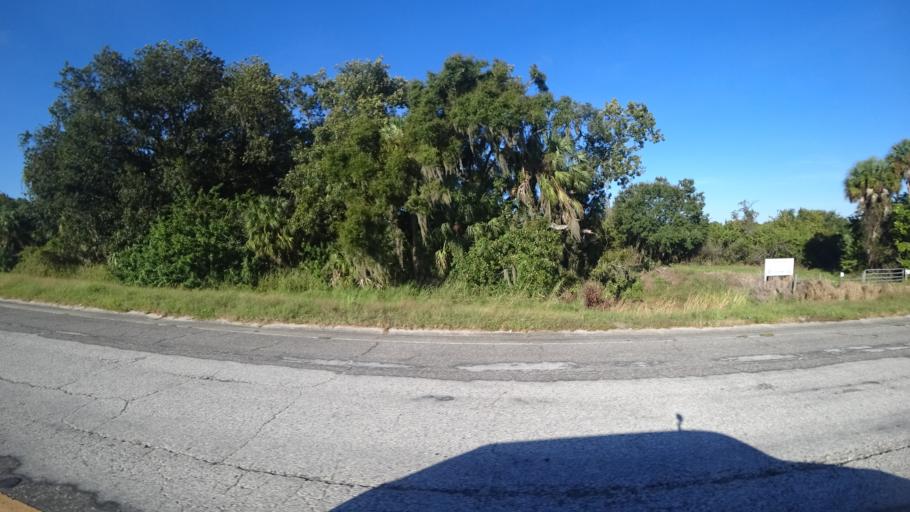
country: US
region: Florida
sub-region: Manatee County
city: Memphis
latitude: 27.5880
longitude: -82.5273
